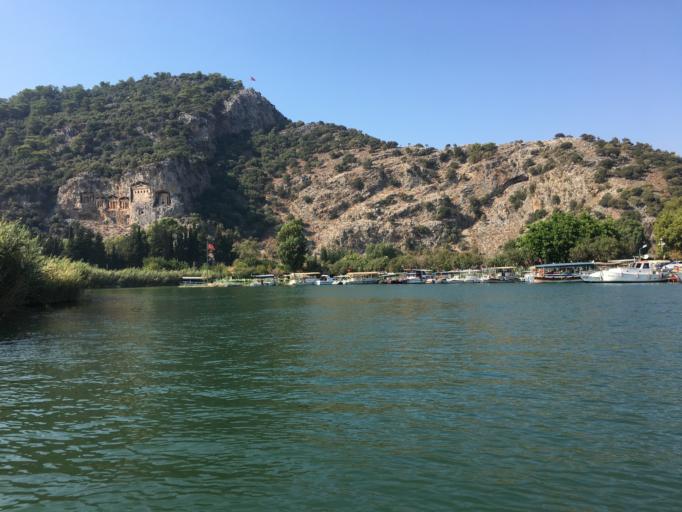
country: TR
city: Dalyan
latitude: 36.8309
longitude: 28.6380
